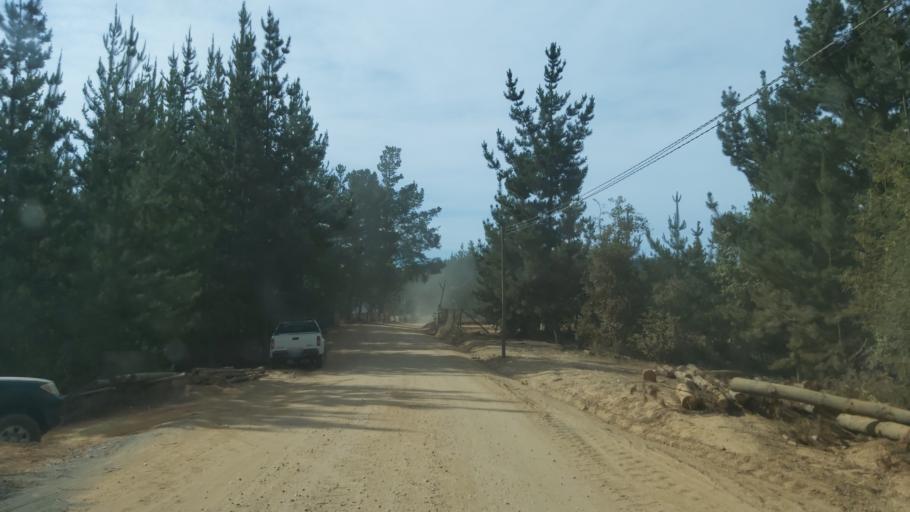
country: CL
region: Maule
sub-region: Provincia de Talca
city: Constitucion
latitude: -34.8463
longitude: -72.0374
